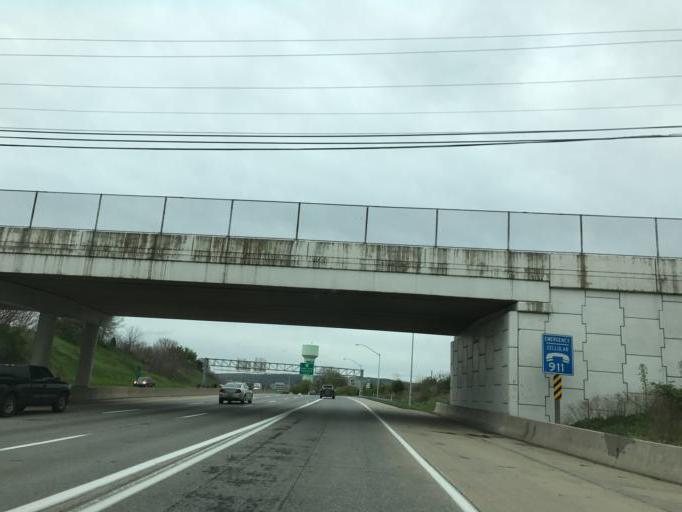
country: US
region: Pennsylvania
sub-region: Lehigh County
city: Dorneyville
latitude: 40.5700
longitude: -75.5350
